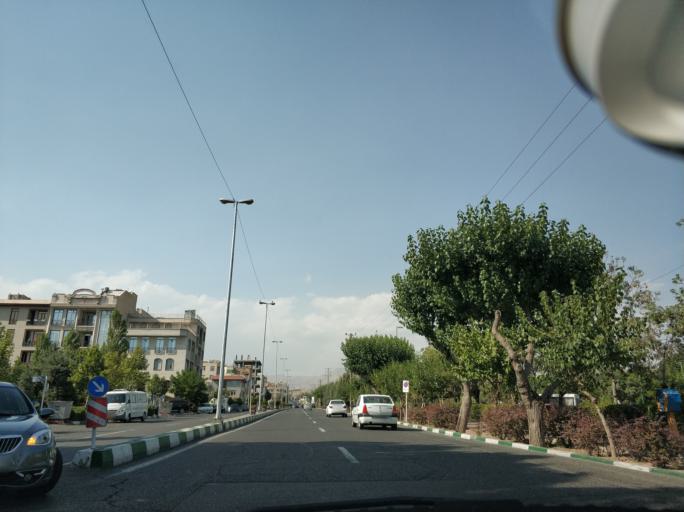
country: IR
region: Tehran
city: Tajrish
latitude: 35.7558
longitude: 51.5392
